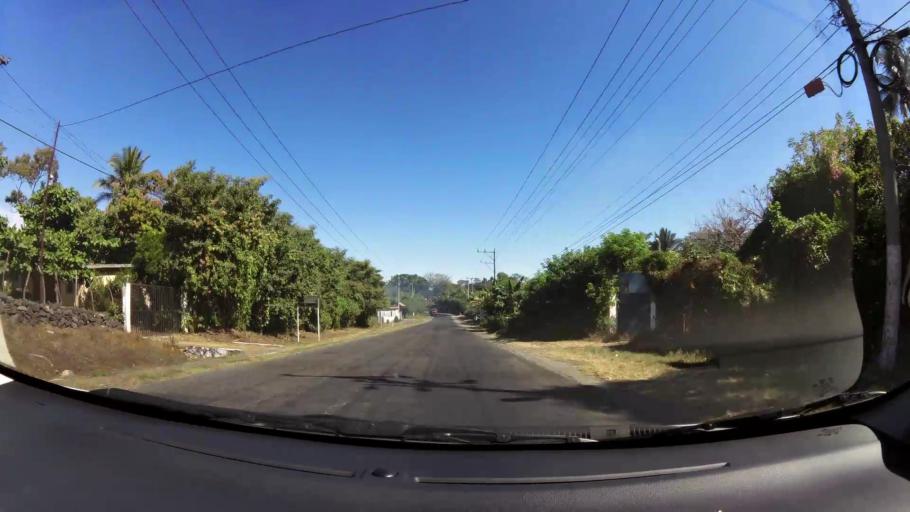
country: SV
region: La Libertad
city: San Juan Opico
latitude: 13.8238
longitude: -89.3540
